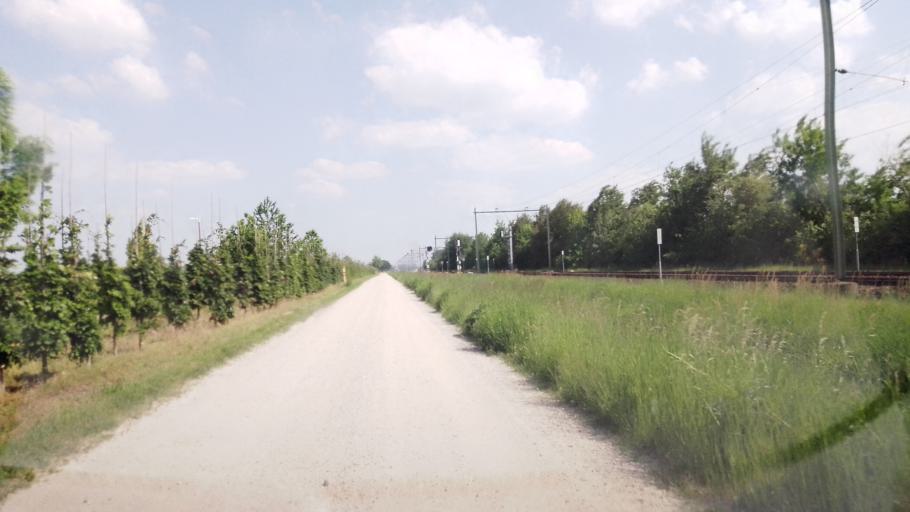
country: NL
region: Limburg
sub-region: Gemeente Peel en Maas
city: Maasbree
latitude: 51.4206
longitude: 6.0548
